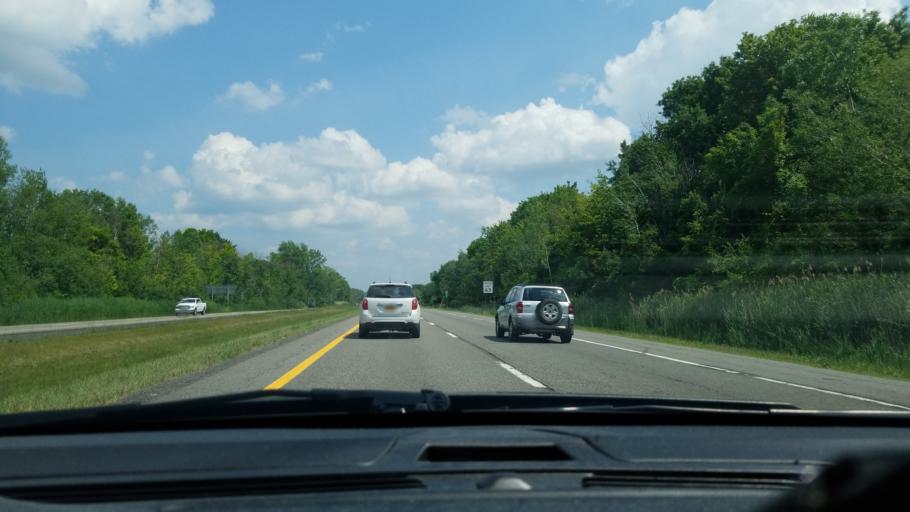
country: US
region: New York
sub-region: Onondaga County
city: Liverpool
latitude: 43.1803
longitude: -76.2254
